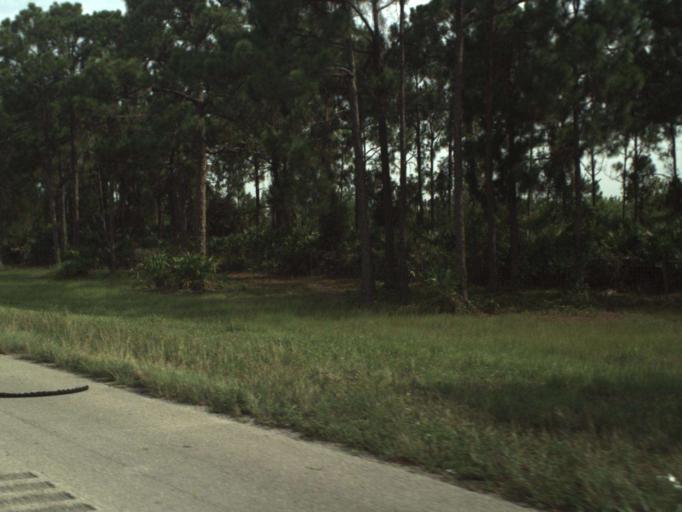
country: US
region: Florida
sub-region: Saint Lucie County
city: Port Saint Lucie
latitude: 27.2391
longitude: -80.4117
